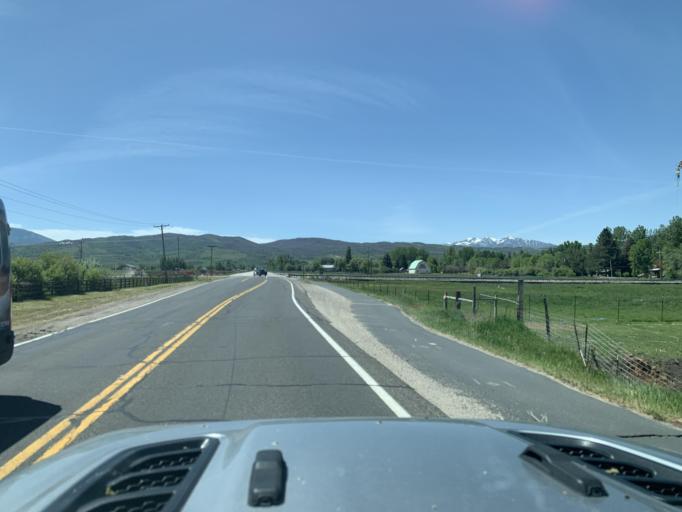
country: US
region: Utah
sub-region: Weber County
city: Wolf Creek
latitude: 41.2640
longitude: -111.7616
